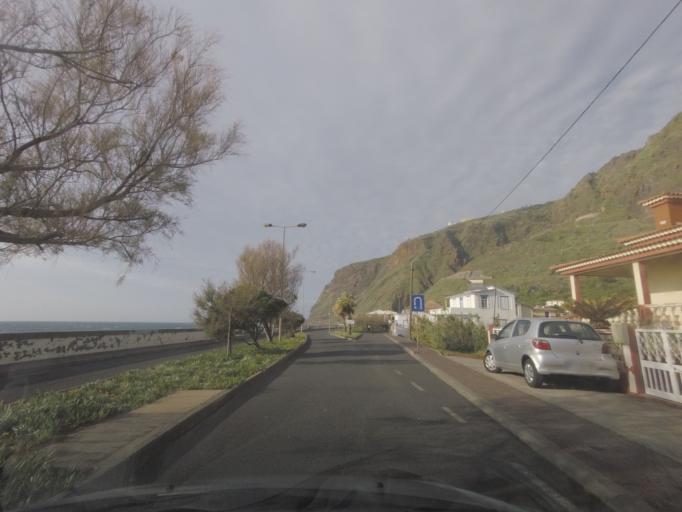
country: PT
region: Madeira
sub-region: Calheta
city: Faja da Ovelha
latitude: 32.7590
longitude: -17.2315
